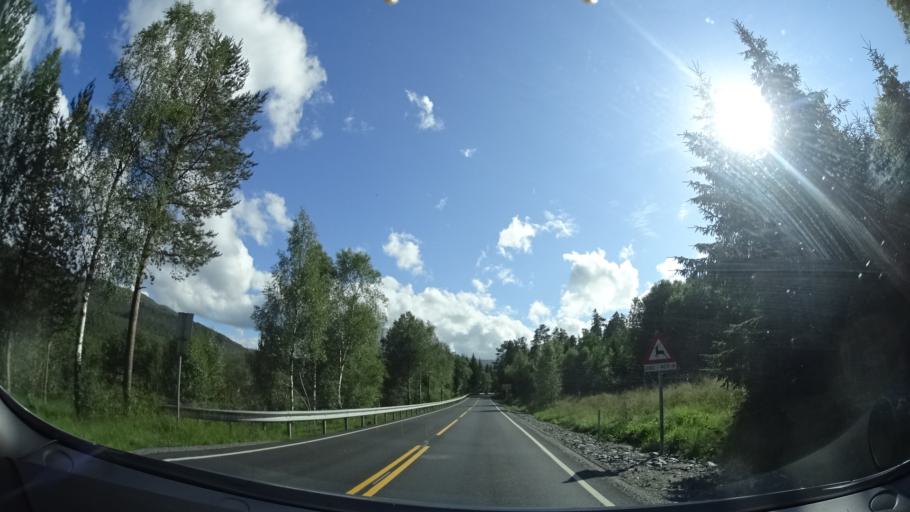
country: NO
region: Sor-Trondelag
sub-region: Hemne
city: Kyrksaeterora
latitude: 63.2109
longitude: 9.0201
